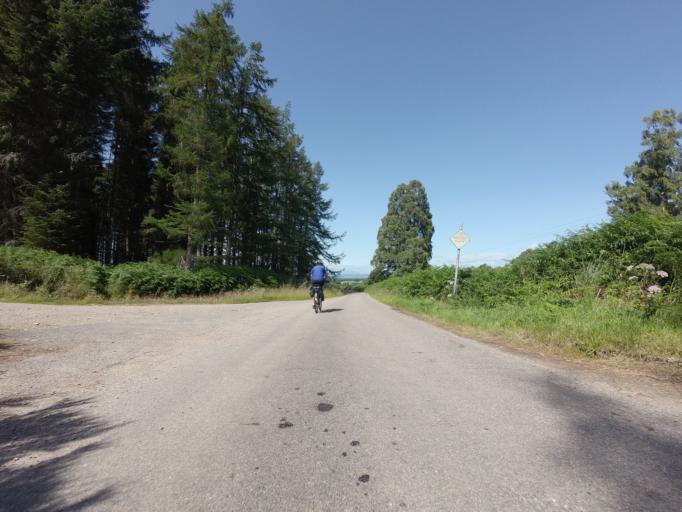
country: GB
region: Scotland
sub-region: Highland
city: Nairn
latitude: 57.5004
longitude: -3.9729
